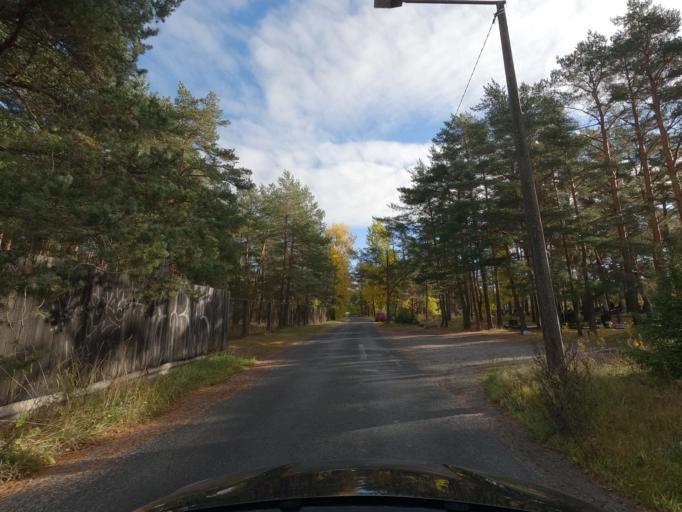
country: EE
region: Harju
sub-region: Tallinna linn
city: Tallinn
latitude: 59.3948
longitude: 24.7123
